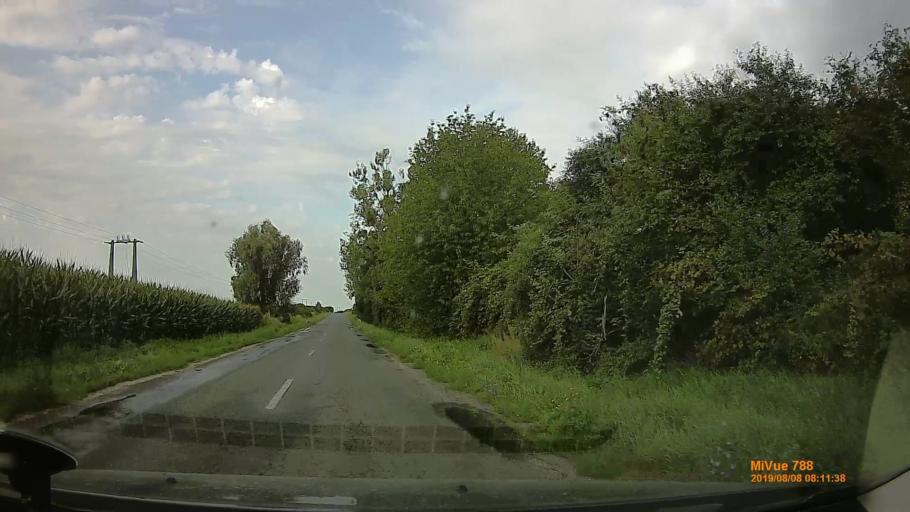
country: HU
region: Zala
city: Murakeresztur
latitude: 46.4212
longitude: 16.8795
